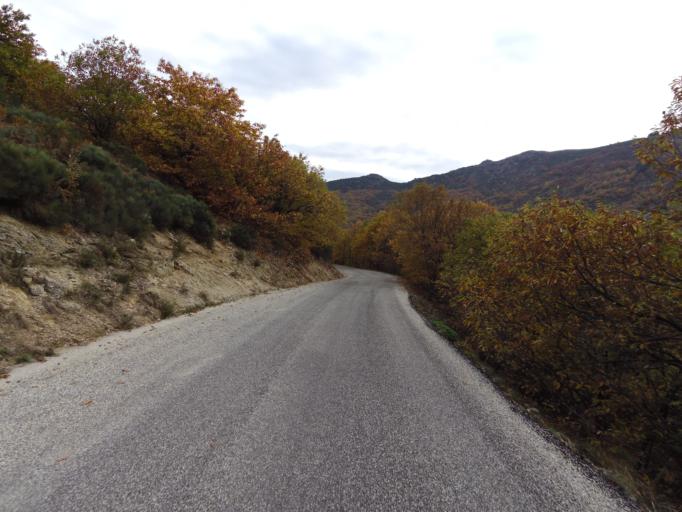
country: FR
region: Rhone-Alpes
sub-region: Departement de l'Ardeche
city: Les Vans
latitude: 44.4995
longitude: 4.0383
